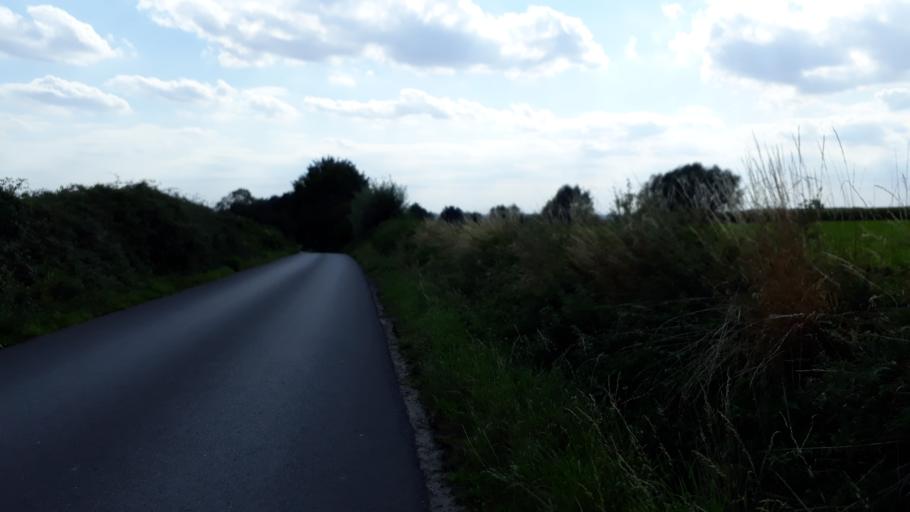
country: BE
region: Flanders
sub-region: Provincie West-Vlaanderen
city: Torhout
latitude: 51.0785
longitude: 3.0812
